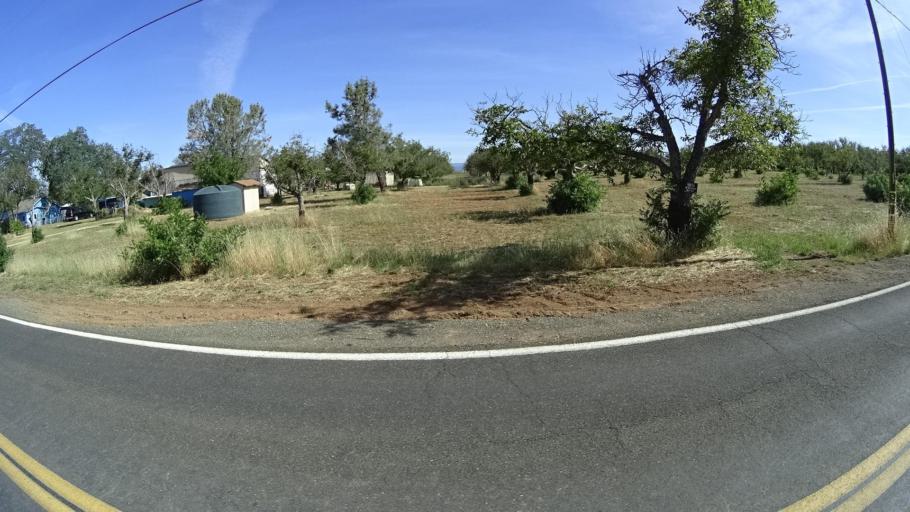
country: US
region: California
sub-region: Lake County
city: Kelseyville
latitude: 38.9750
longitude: -122.8516
